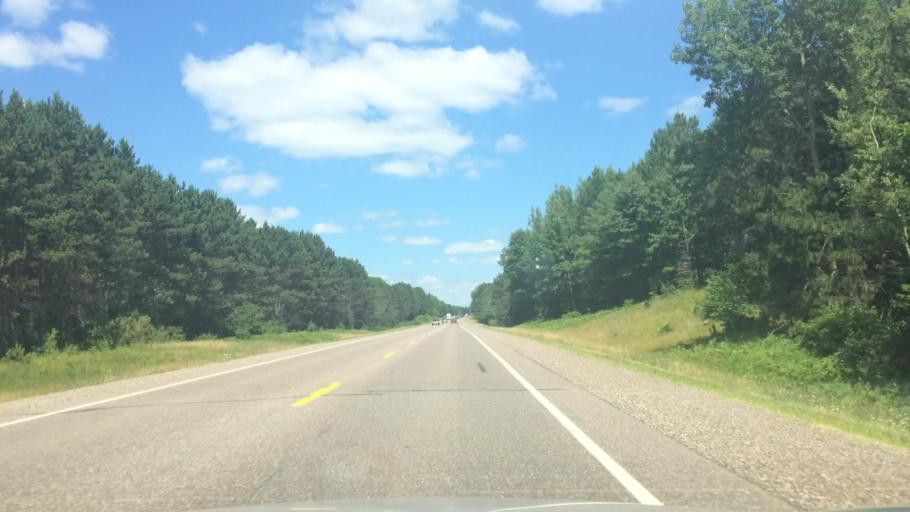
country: US
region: Wisconsin
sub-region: Vilas County
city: Lac du Flambeau
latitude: 45.9633
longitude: -89.7001
